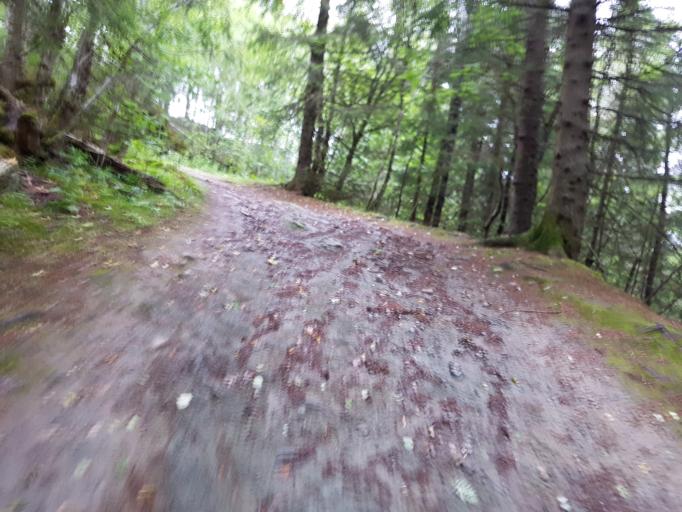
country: NO
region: Sor-Trondelag
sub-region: Trondheim
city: Trondheim
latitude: 63.3987
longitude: 10.4669
